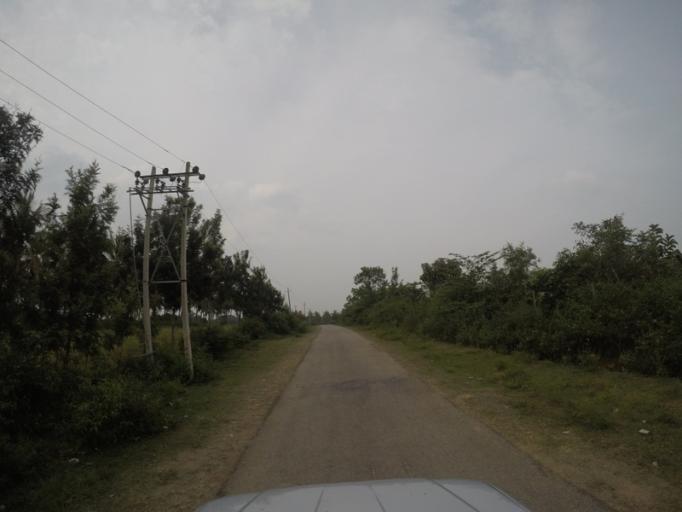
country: IN
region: Karnataka
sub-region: Hassan
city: Belur
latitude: 13.1580
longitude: 75.9333
